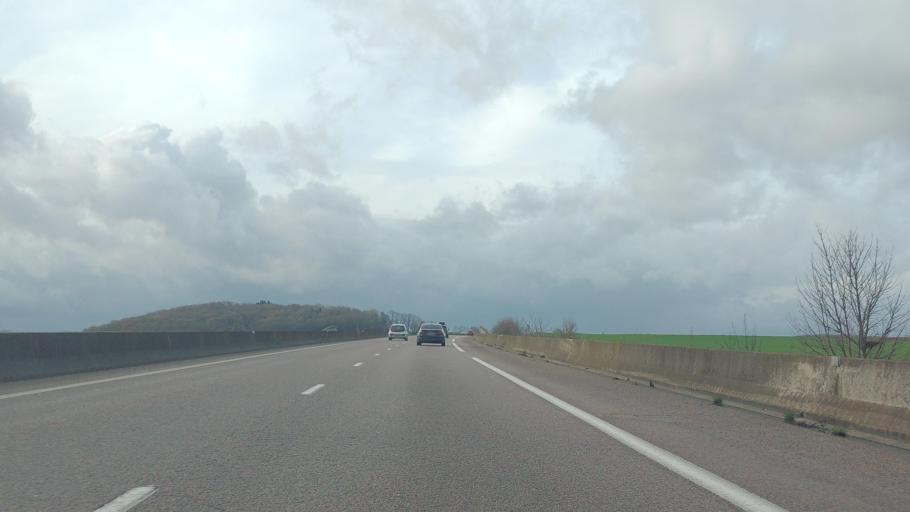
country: FR
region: Picardie
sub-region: Departement de l'Oise
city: Bailleul-sur-Therain
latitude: 49.4126
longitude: 2.1931
